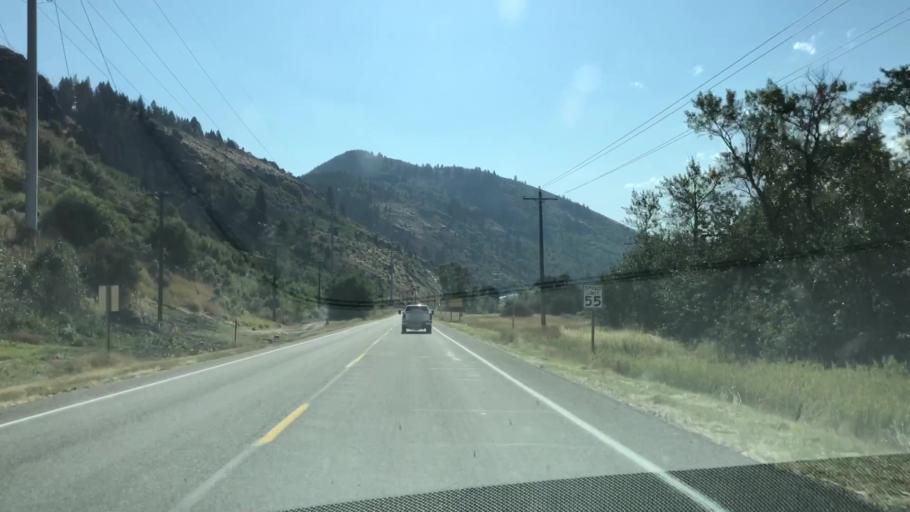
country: US
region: Idaho
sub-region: Teton County
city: Victor
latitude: 43.3487
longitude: -111.2140
